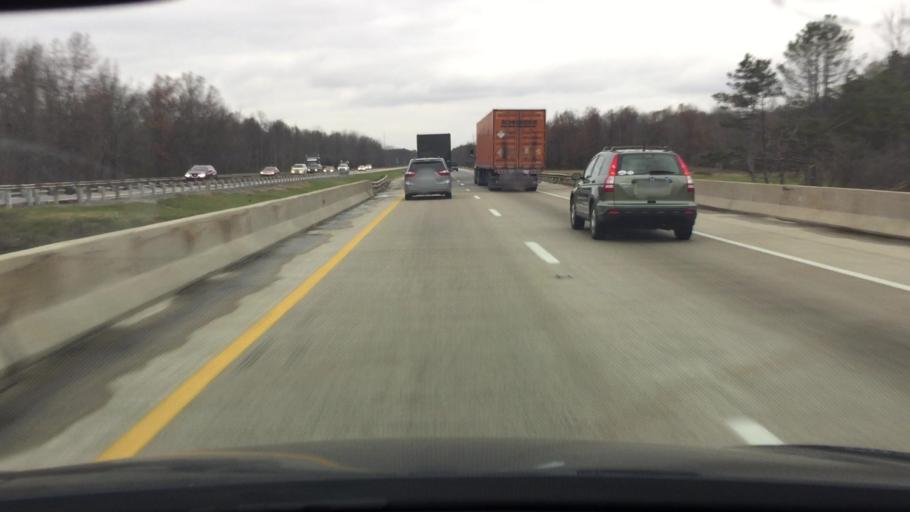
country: US
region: Ohio
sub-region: Mahoning County
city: Boardman
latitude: 40.9922
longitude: -80.6913
